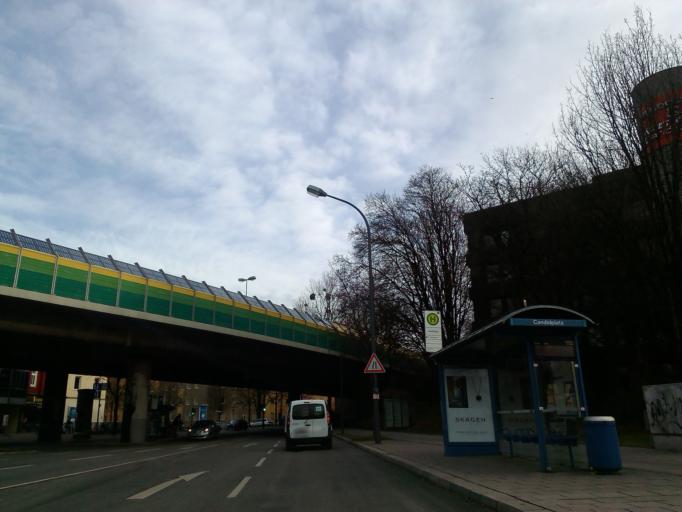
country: DE
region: Bavaria
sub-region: Upper Bavaria
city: Munich
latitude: 48.1115
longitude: 11.5701
